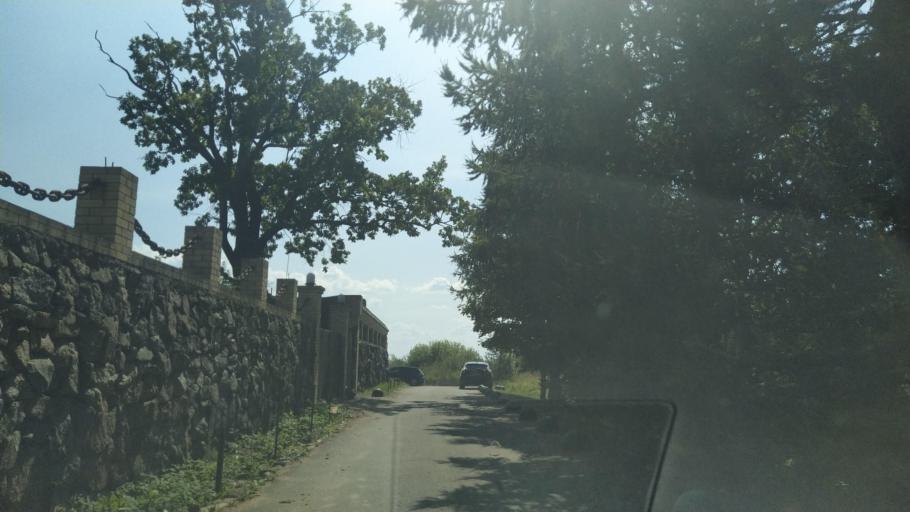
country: RU
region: St.-Petersburg
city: Lakhtinskiy
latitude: 59.9888
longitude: 30.1570
